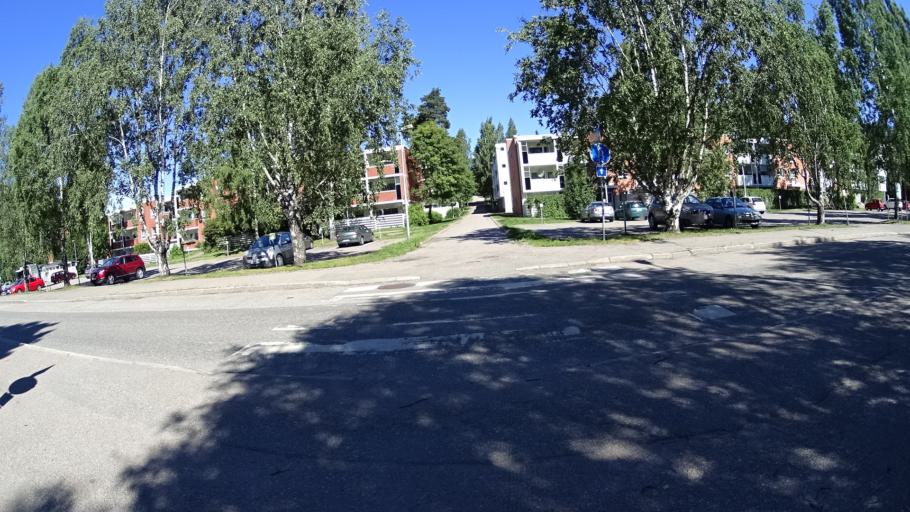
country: FI
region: Uusimaa
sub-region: Helsinki
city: Koukkuniemi
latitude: 60.1533
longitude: 24.7318
